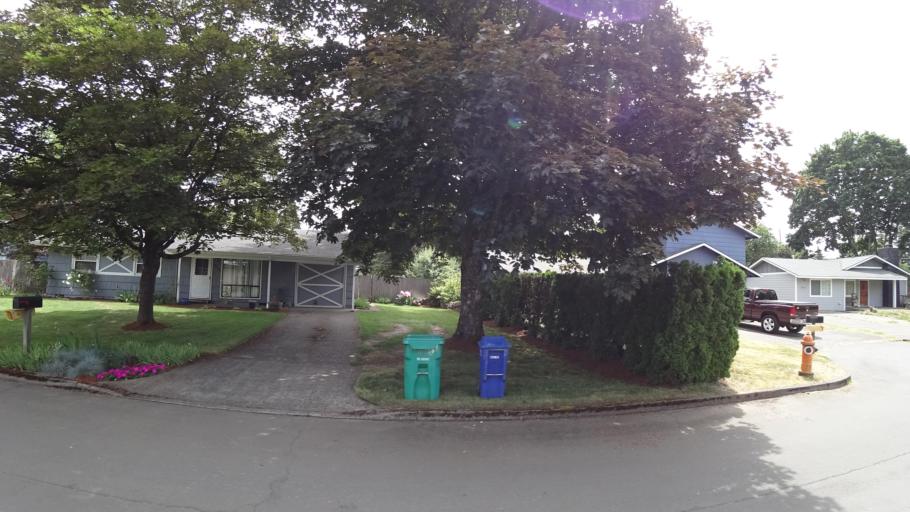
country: US
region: Oregon
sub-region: Multnomah County
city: Lents
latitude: 45.4928
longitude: -122.5311
